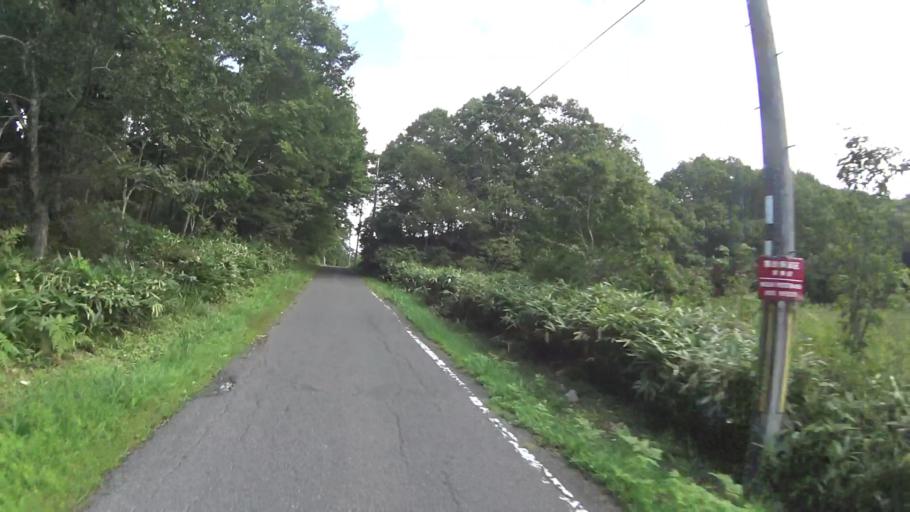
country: JP
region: Kyoto
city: Miyazu
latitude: 35.6500
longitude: 135.1802
